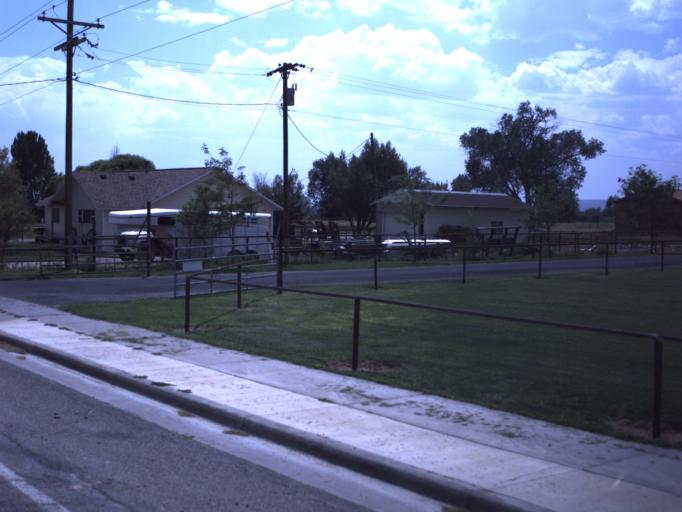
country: US
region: Utah
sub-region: Duchesne County
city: Roosevelt
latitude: 40.4292
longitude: -110.0301
